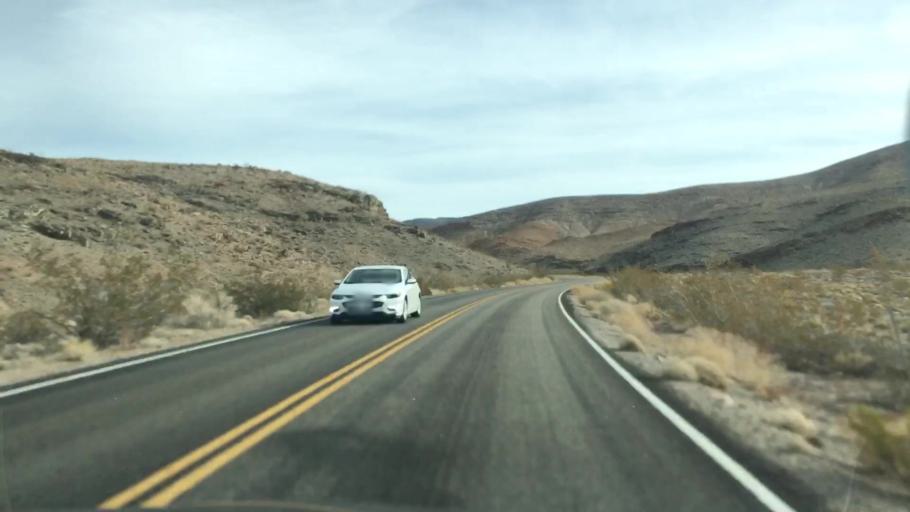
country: US
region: Nevada
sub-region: Nye County
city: Beatty
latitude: 36.7430
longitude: -116.9615
